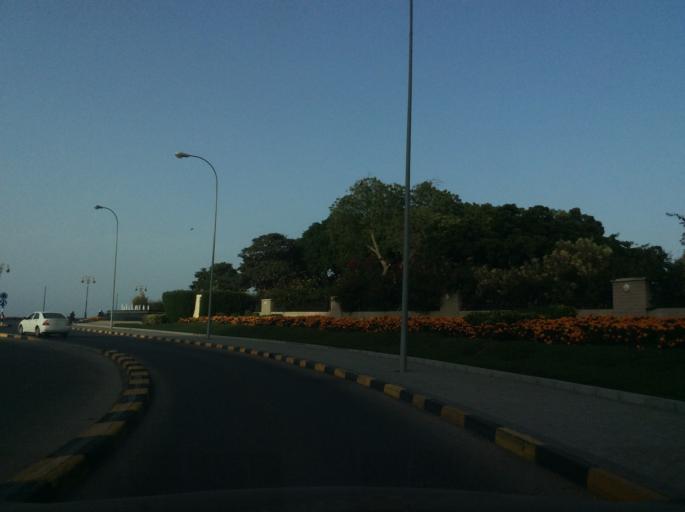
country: OM
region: Muhafazat Masqat
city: Muscat
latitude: 23.6214
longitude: 58.5768
